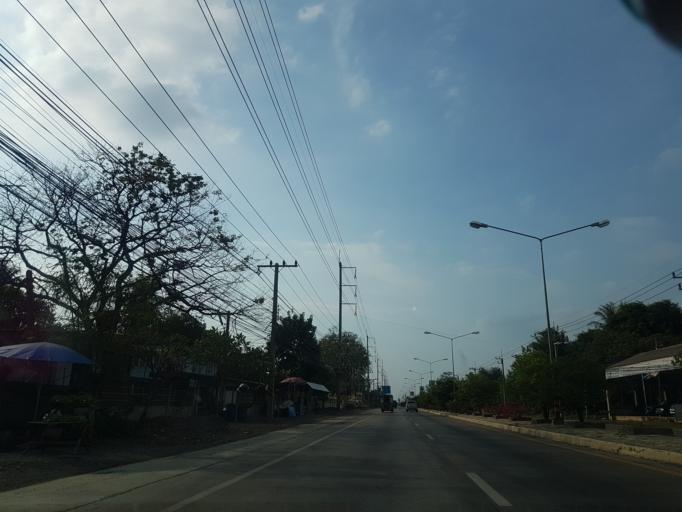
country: TH
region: Lop Buri
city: Lop Buri
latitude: 14.7654
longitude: 100.7138
